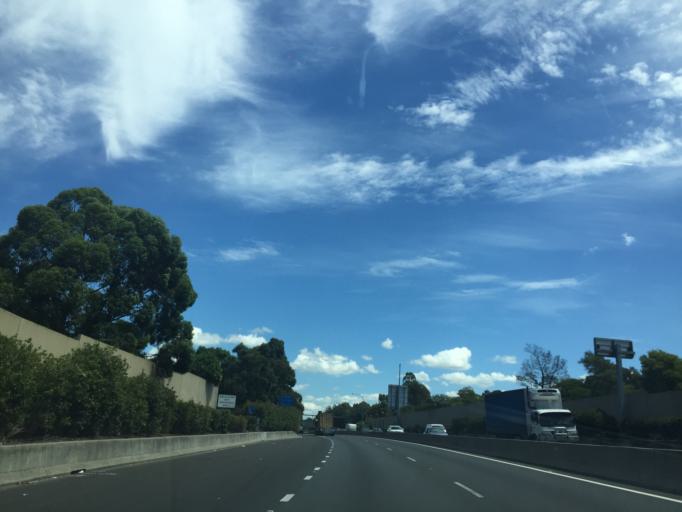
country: AU
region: New South Wales
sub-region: Canterbury
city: Clemton Park
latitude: -33.9405
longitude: 151.0846
